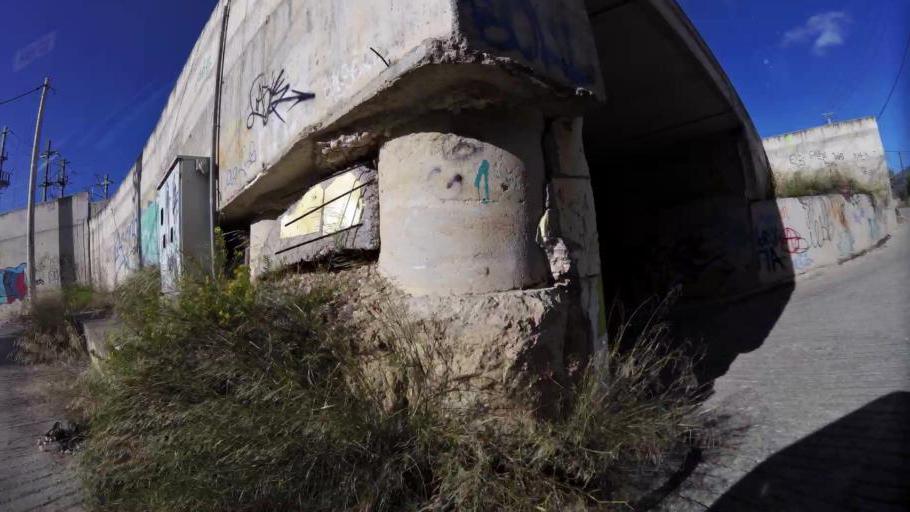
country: GR
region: Attica
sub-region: Nomarchia Anatolikis Attikis
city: Acharnes
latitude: 38.0719
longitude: 23.7372
